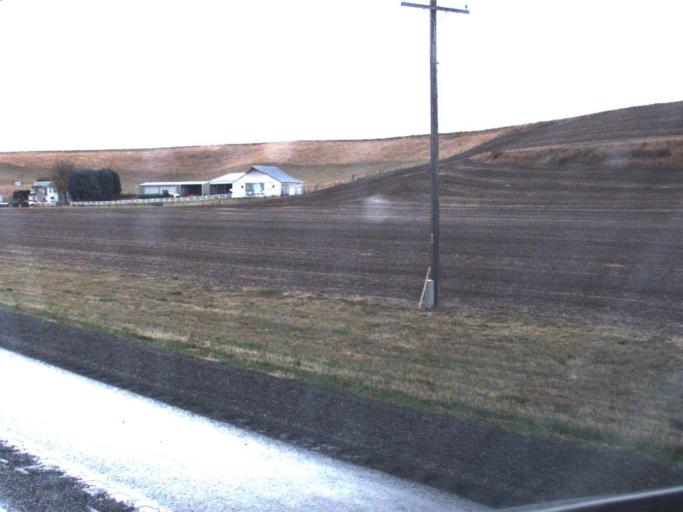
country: US
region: Washington
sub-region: Asotin County
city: Clarkston
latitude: 46.5621
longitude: -117.1098
